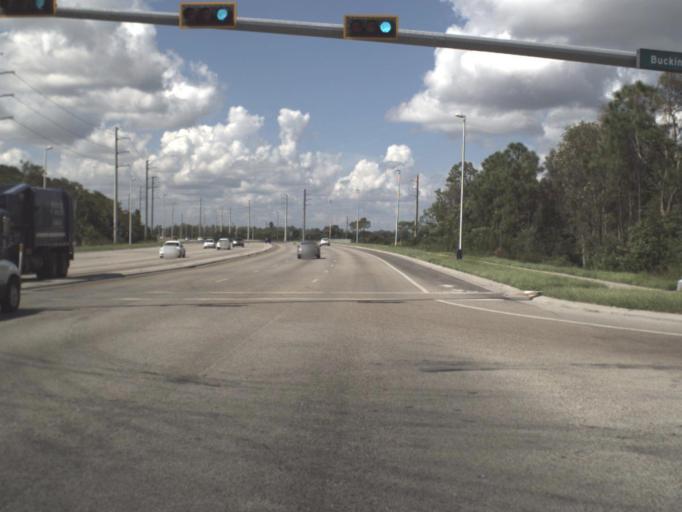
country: US
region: Florida
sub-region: Lee County
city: Gateway
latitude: 26.6260
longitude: -81.7762
